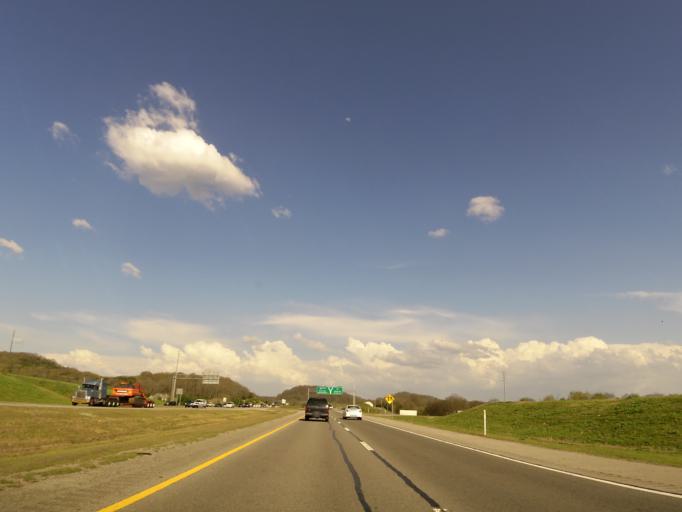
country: US
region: Tennessee
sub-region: Williamson County
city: Thompson's Station
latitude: 35.8217
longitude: -86.8542
